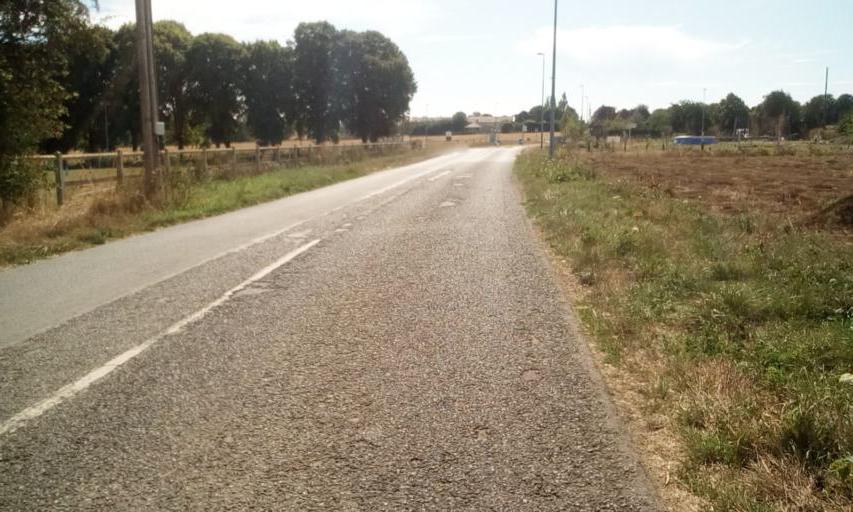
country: FR
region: Lower Normandy
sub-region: Departement du Calvados
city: Eterville
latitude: 49.1352
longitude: -0.4117
